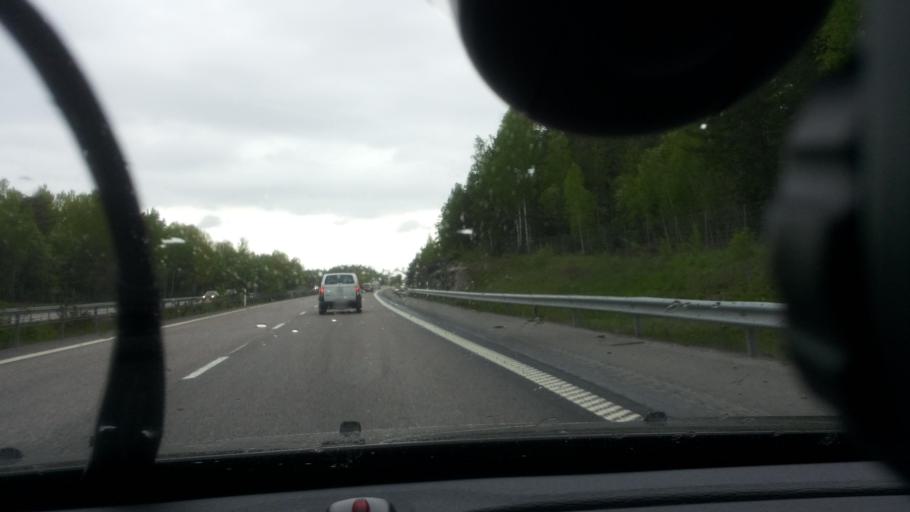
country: SE
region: Uppsala
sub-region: Knivsta Kommun
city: Knivsta
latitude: 59.7103
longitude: 17.8498
